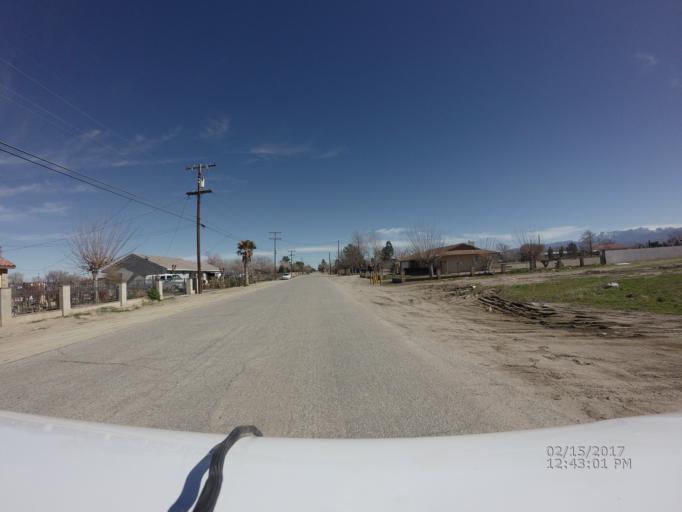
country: US
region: California
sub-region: Los Angeles County
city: Littlerock
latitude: 34.5760
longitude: -117.9678
